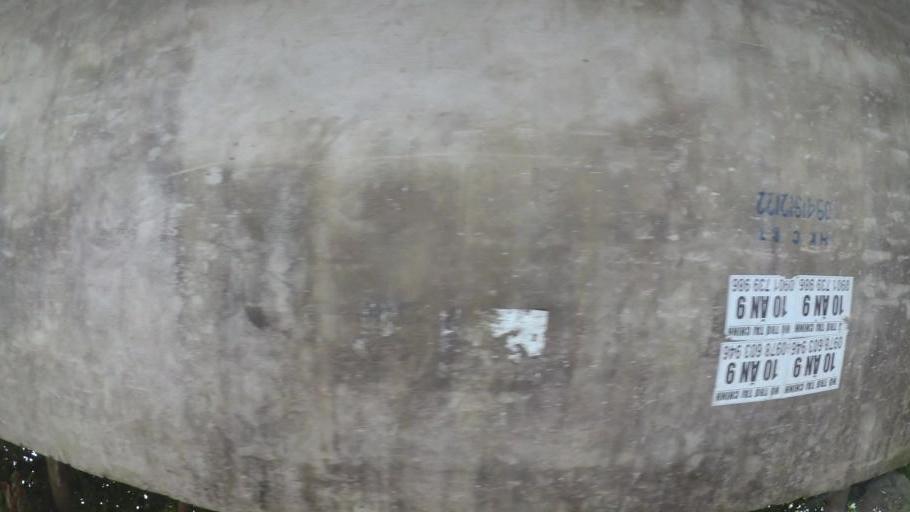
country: VN
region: Ha Noi
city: Ha Dong
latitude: 20.9906
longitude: 105.7371
